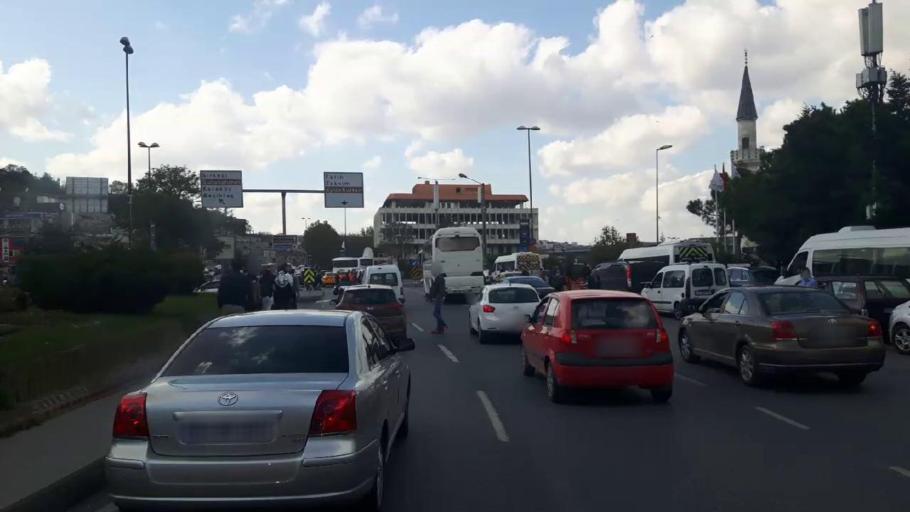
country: TR
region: Istanbul
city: Eminoenue
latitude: 41.0184
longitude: 28.9690
